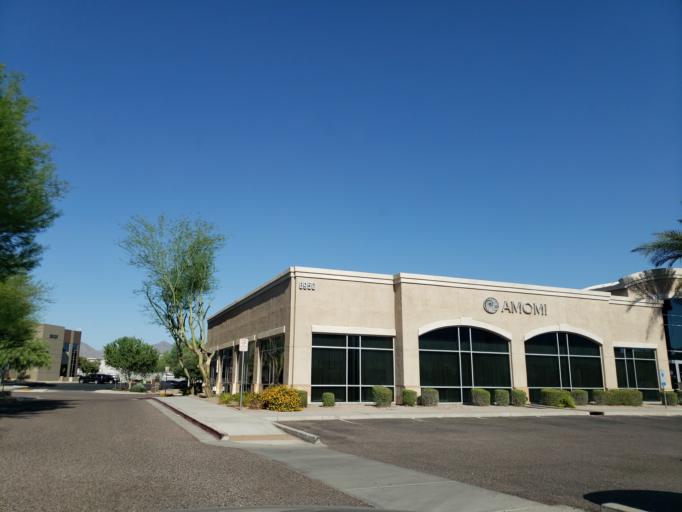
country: US
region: Arizona
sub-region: Maricopa County
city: Paradise Valley
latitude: 33.6525
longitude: -111.9310
